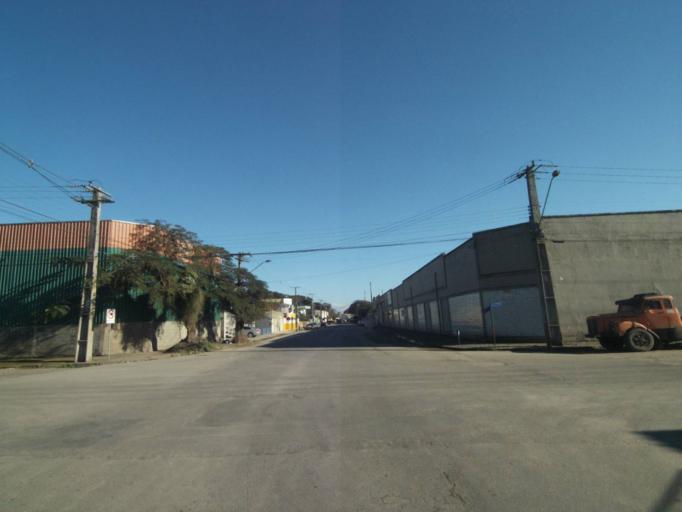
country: BR
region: Parana
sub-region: Paranagua
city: Paranagua
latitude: -25.5131
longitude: -48.5125
